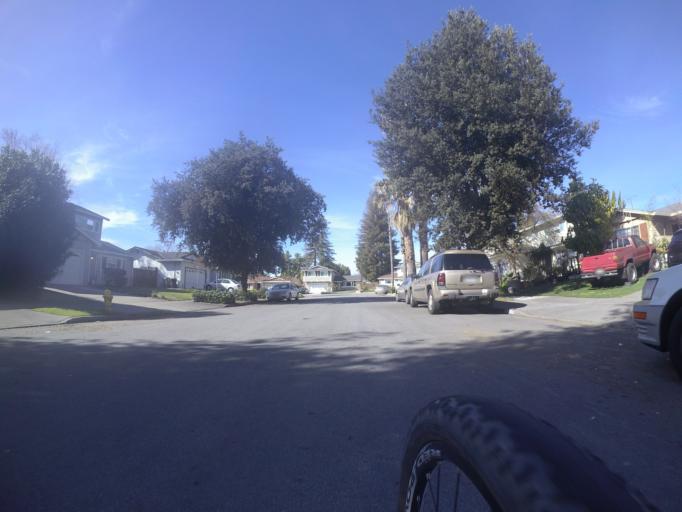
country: US
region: California
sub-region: Santa Clara County
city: Milpitas
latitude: 37.4156
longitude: -121.8606
